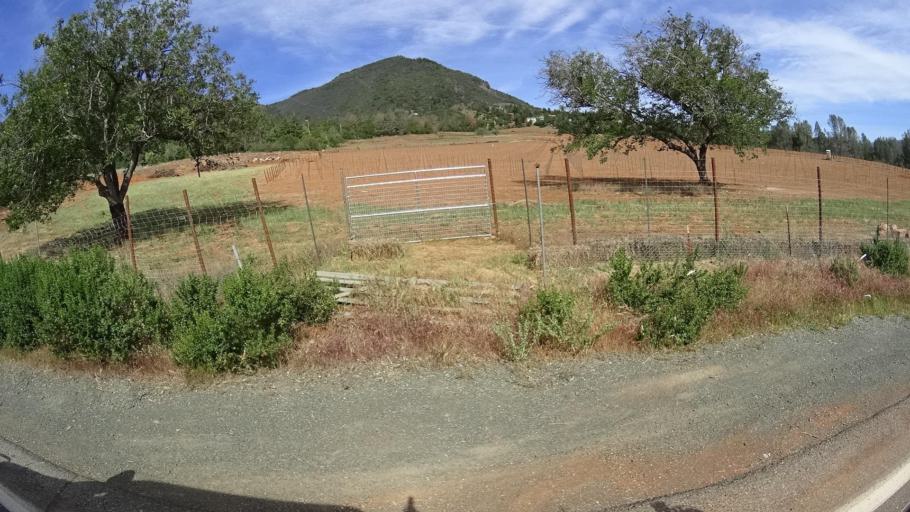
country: US
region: California
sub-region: Lake County
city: Soda Bay
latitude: 38.9842
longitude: -122.7419
